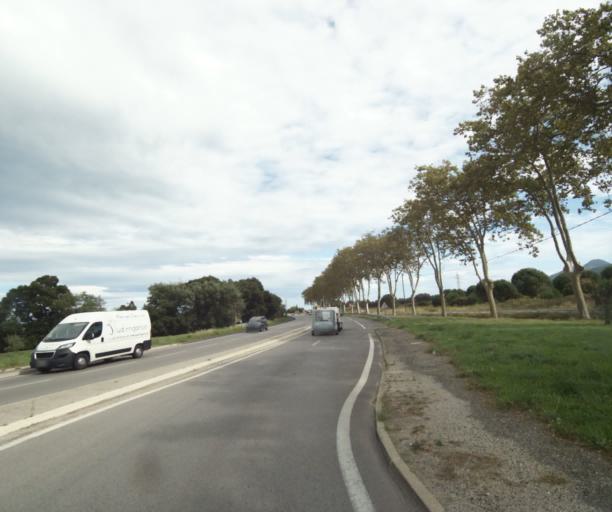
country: FR
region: Languedoc-Roussillon
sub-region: Departement des Pyrenees-Orientales
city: Argelers
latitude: 42.5510
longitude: 2.9976
